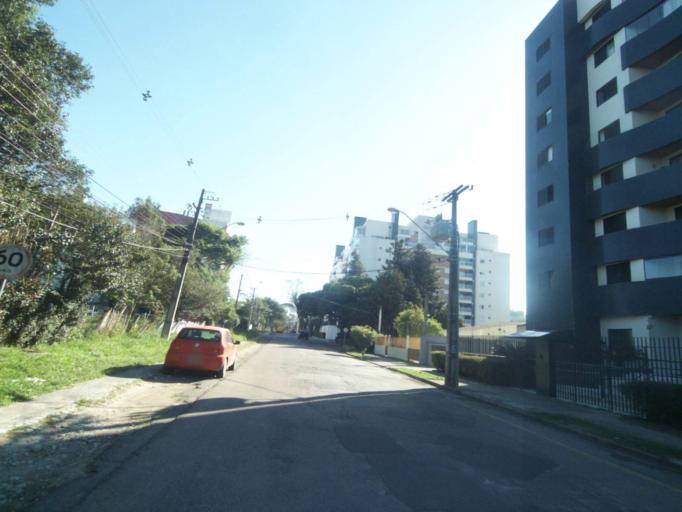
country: BR
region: Parana
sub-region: Curitiba
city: Curitiba
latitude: -25.3936
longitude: -49.2301
